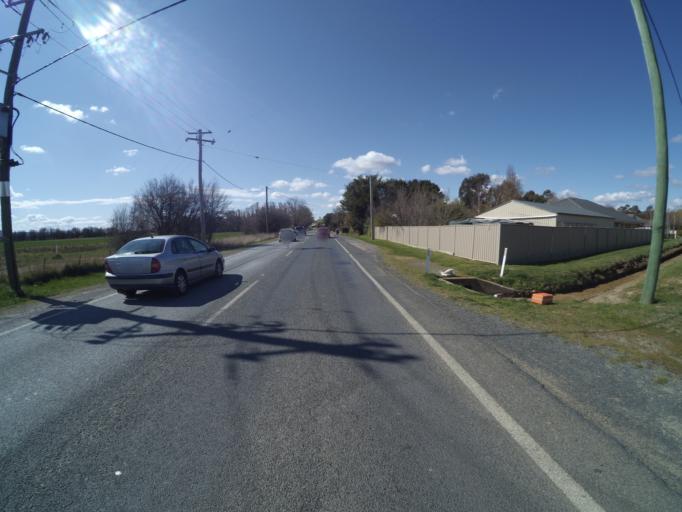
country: AU
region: New South Wales
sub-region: Palerang
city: Bungendore
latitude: -35.2596
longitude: 149.4364
